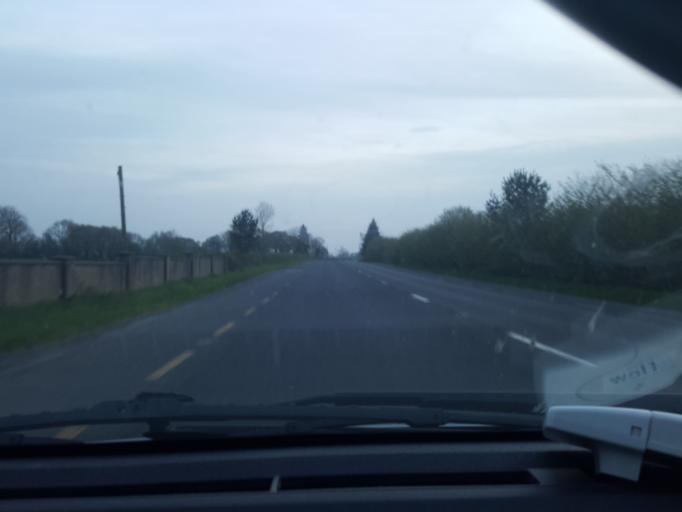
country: IE
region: Munster
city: Cahir
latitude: 52.3595
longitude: -7.9851
